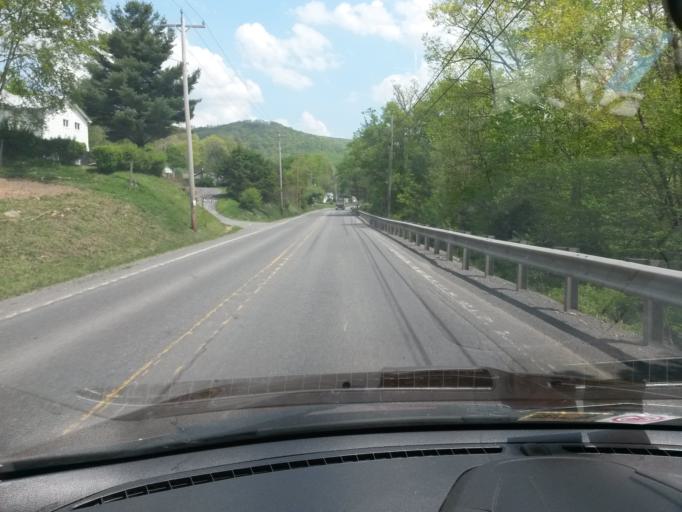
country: US
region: West Virginia
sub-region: Greenbrier County
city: Rainelle
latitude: 37.9860
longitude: -80.7249
